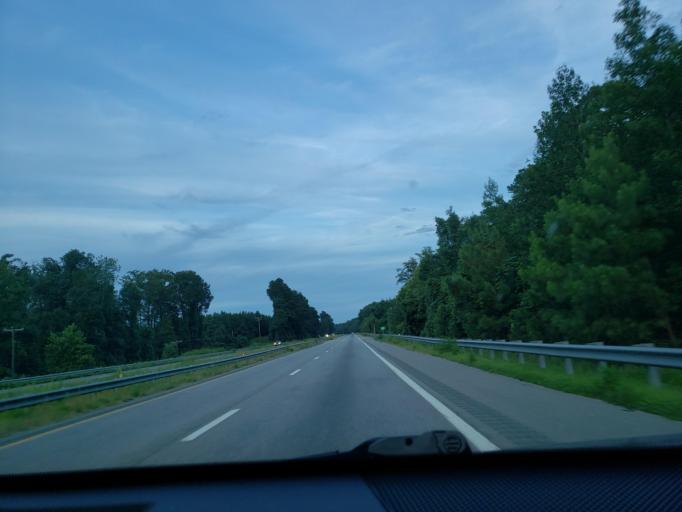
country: US
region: Virginia
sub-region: Southampton County
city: Courtland
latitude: 36.7022
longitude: -77.2522
